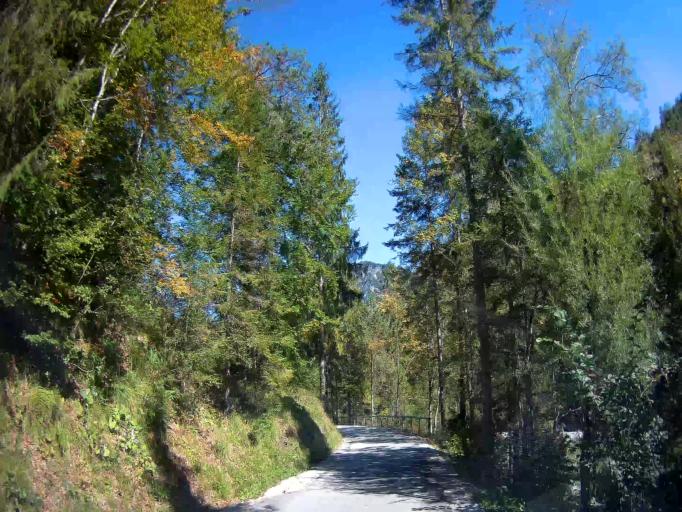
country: AT
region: Salzburg
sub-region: Politischer Bezirk Zell am See
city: Sankt Martin bei Lofer
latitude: 47.5295
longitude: 12.7162
